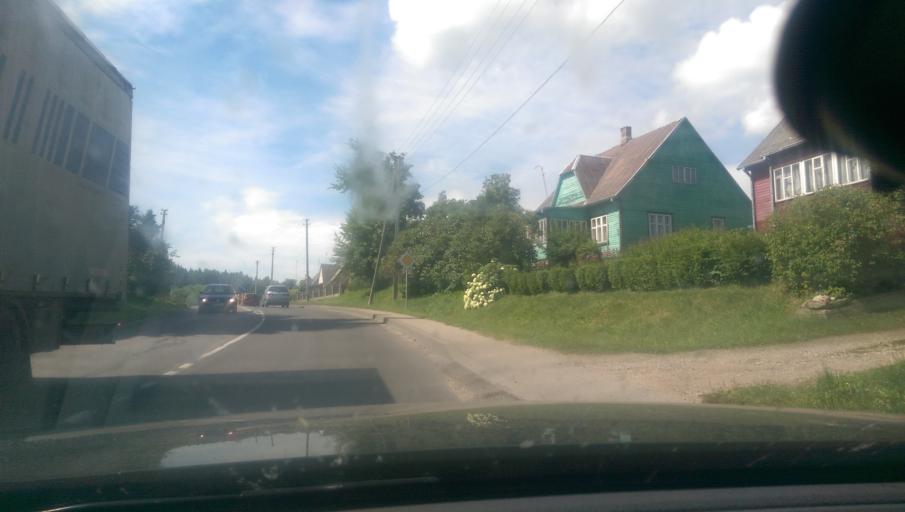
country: LT
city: Prienai
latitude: 54.6356
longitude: 23.9511
